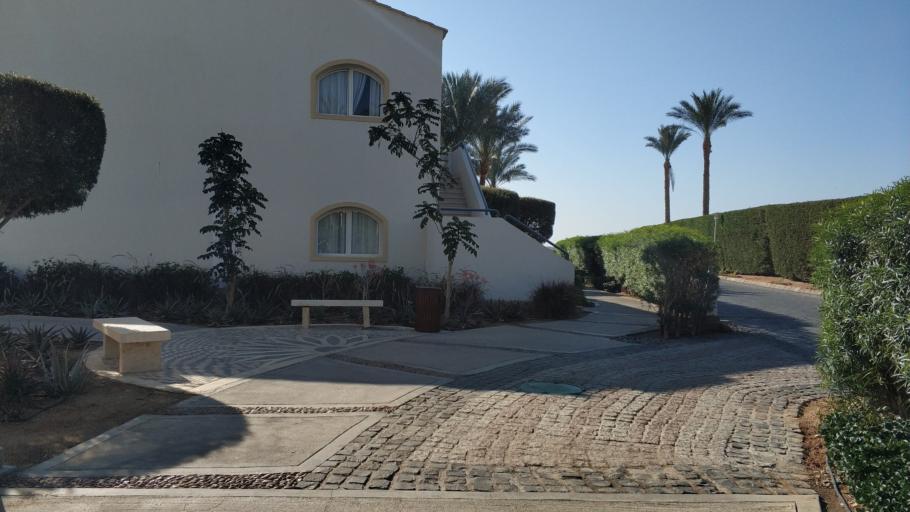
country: EG
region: South Sinai
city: Sharm el-Sheikh
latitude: 27.9175
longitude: 34.3605
